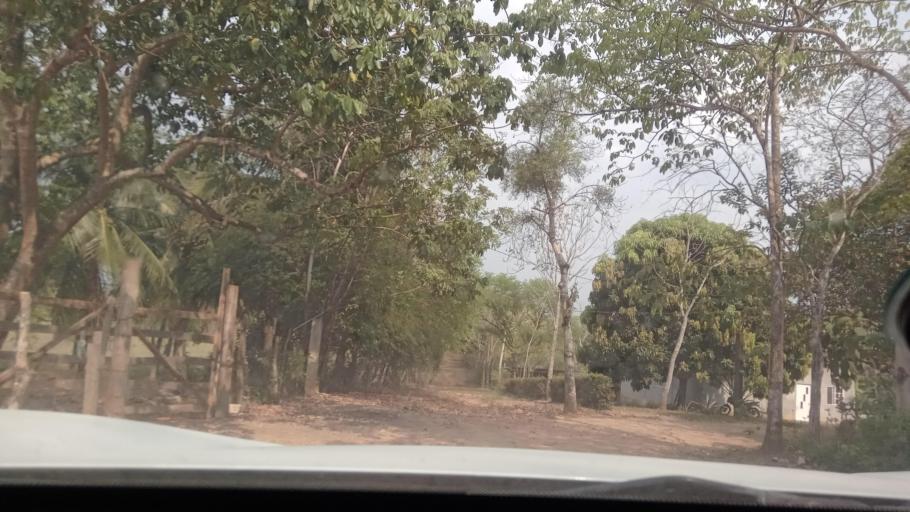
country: MX
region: Tabasco
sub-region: Huimanguillo
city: Francisco Rueda
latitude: 17.6928
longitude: -93.8320
